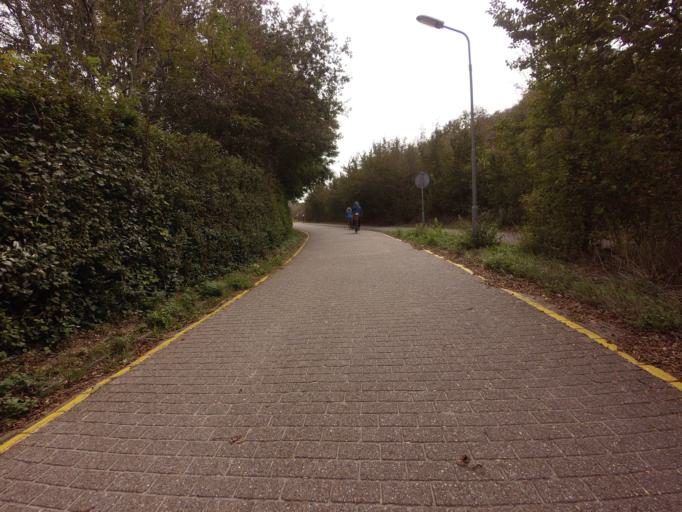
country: NL
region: Zeeland
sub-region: Gemeente Vlissingen
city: Vlissingen
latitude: 51.4958
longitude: 3.4993
